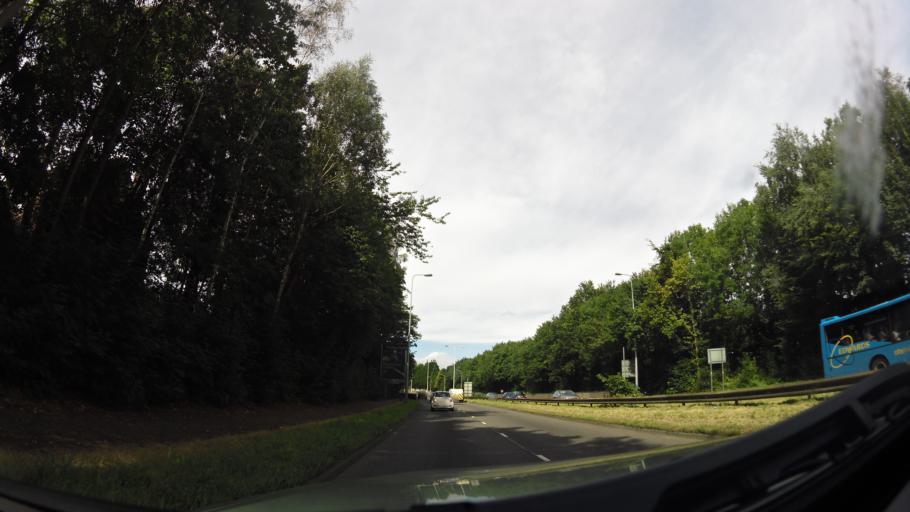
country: GB
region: Wales
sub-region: Cardiff
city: Radyr
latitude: 51.5246
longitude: -3.2316
